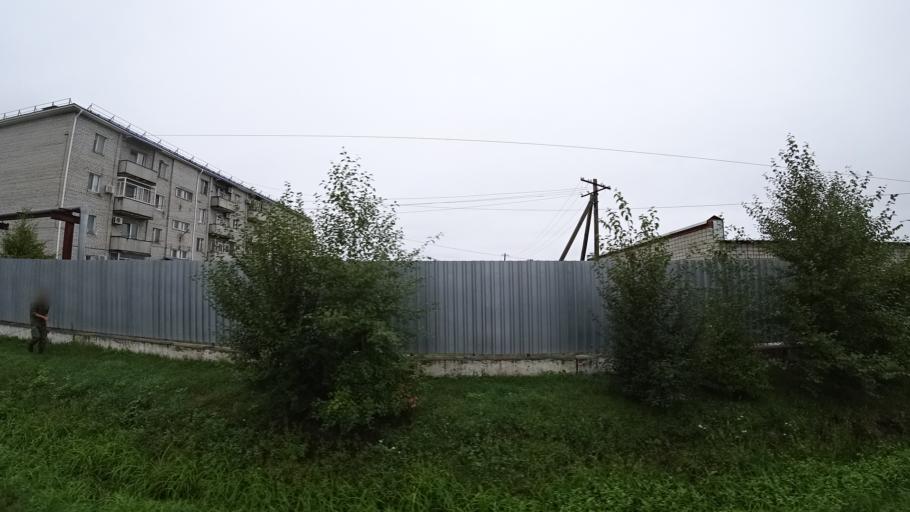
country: RU
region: Primorskiy
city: Monastyrishche
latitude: 44.2083
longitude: 132.4472
